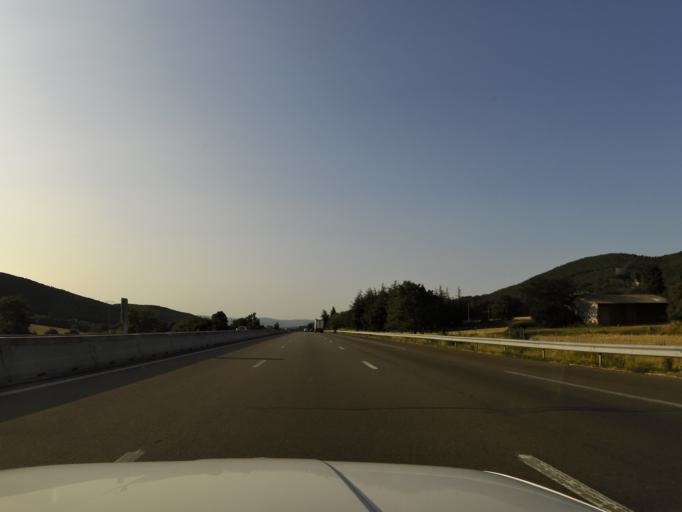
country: FR
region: Rhone-Alpes
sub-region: Departement de la Drome
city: Savasse
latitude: 44.6209
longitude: 4.7929
